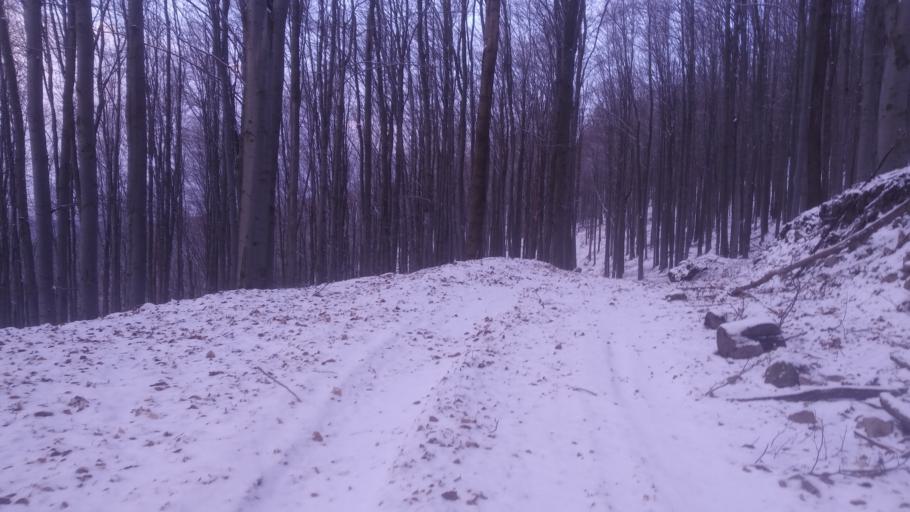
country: SK
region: Nitriansky
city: Sahy
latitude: 47.9684
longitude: 18.9285
